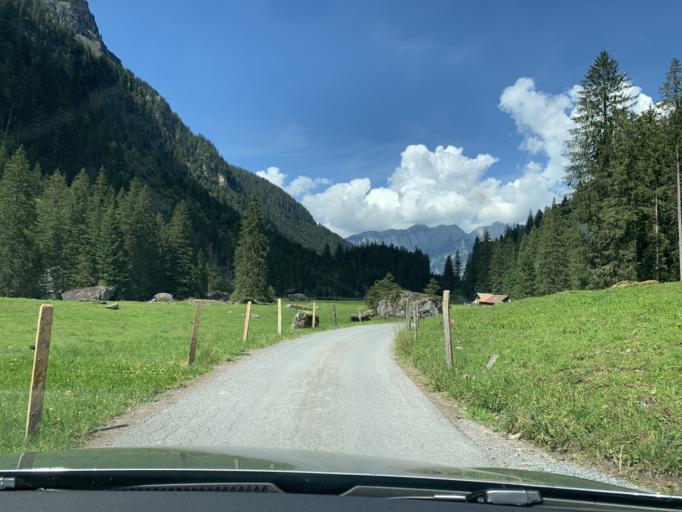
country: CH
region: Saint Gallen
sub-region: Wahlkreis Sarganserland
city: Quarten
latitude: 47.0731
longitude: 9.1978
